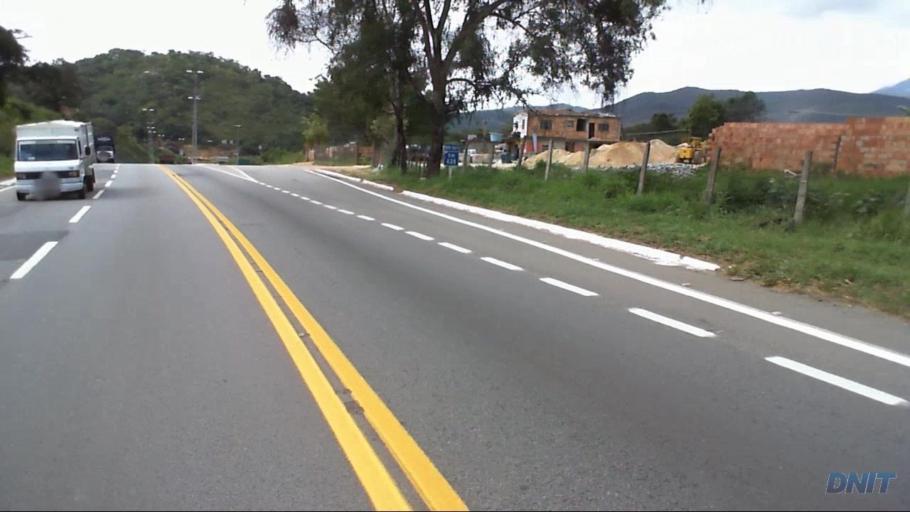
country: BR
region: Minas Gerais
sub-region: Santa Luzia
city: Santa Luzia
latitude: -19.8000
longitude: -43.7576
